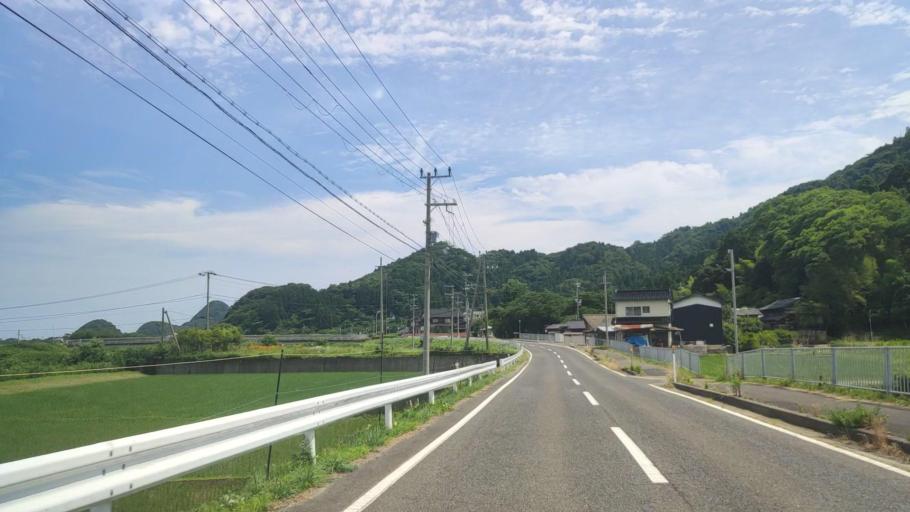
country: JP
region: Hyogo
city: Toyooka
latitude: 35.6466
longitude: 134.7631
